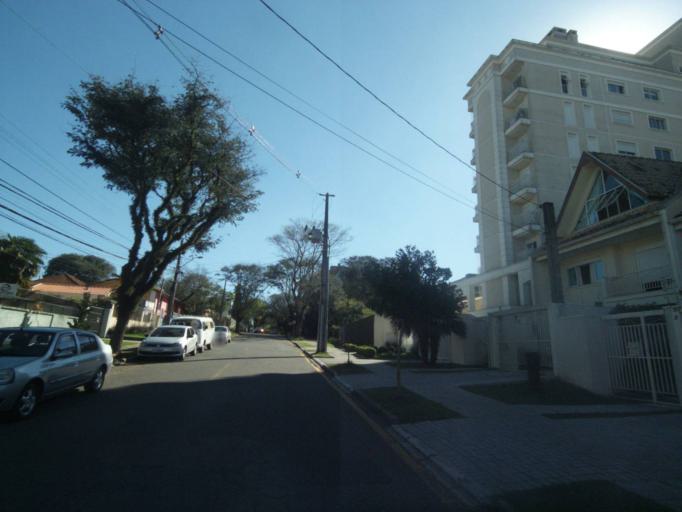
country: BR
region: Parana
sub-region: Curitiba
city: Curitiba
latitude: -25.3999
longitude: -49.2417
